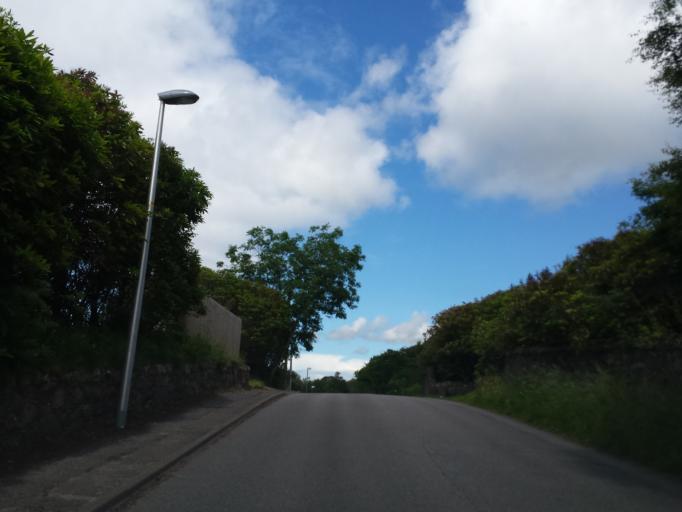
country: GB
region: Scotland
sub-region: Highland
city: Ullapool
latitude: 57.7138
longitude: -5.6804
